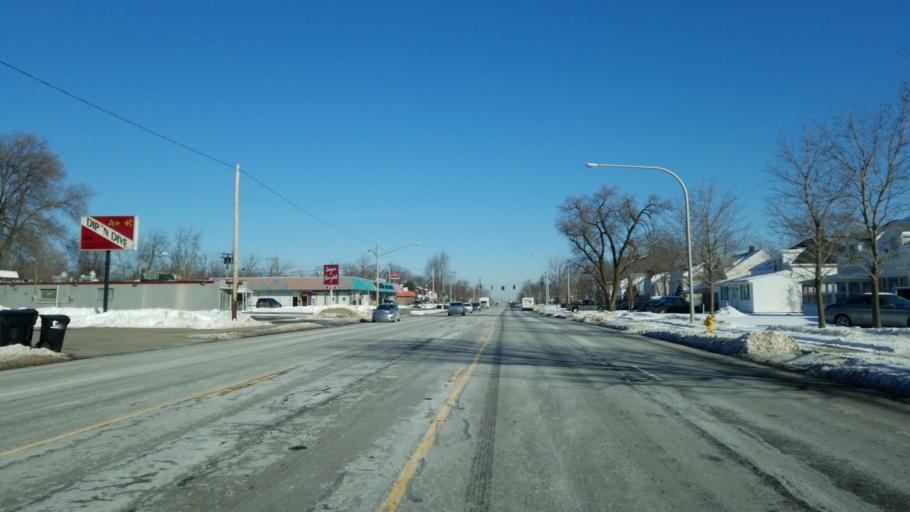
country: US
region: New York
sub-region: Erie County
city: Eggertsville
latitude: 42.9673
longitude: -78.8234
